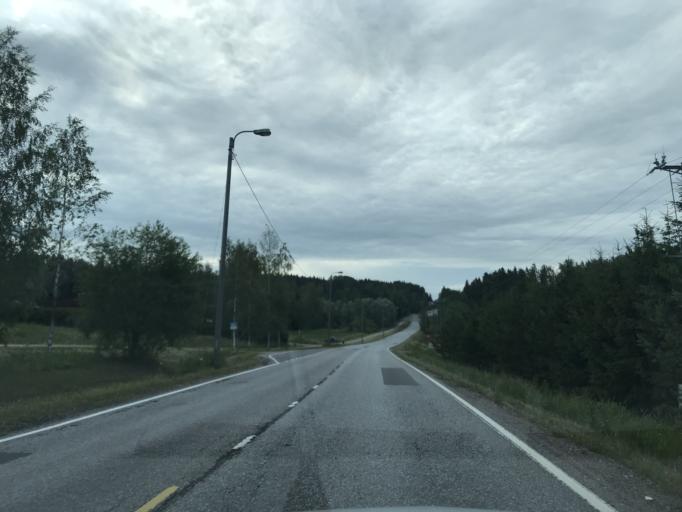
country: FI
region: Uusimaa
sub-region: Helsinki
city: Nurmijaervi
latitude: 60.3832
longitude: 24.6532
